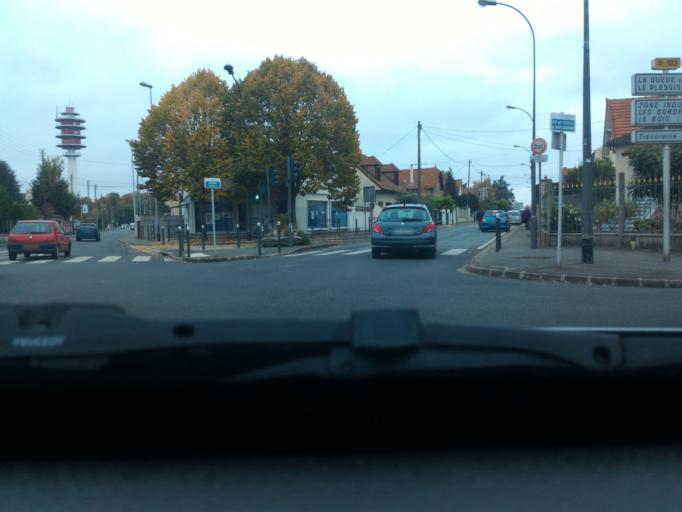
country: FR
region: Ile-de-France
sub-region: Departement du Val-de-Marne
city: Chennevieres-sur-Marne
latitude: 48.7990
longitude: 2.5339
